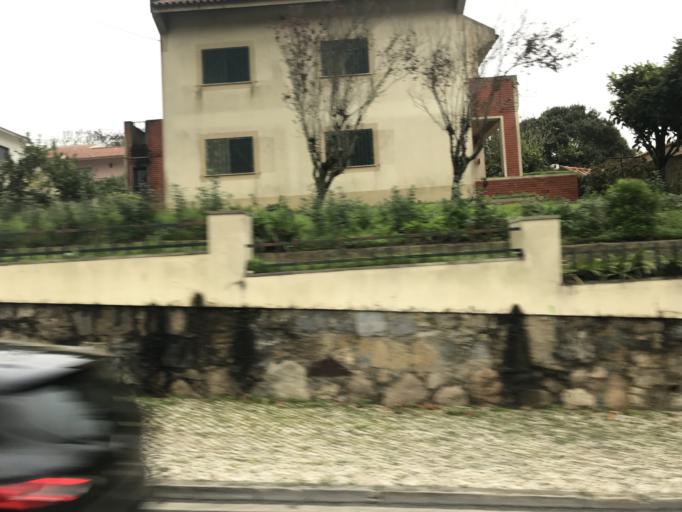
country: PT
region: Lisbon
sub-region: Sintra
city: Sintra
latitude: 38.7905
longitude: -9.3738
